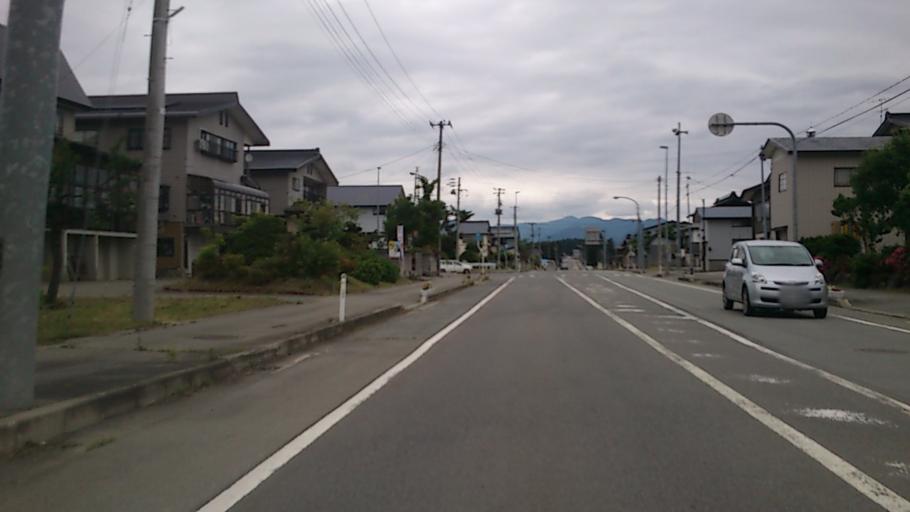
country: JP
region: Yamagata
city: Shinjo
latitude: 38.7009
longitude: 140.3104
